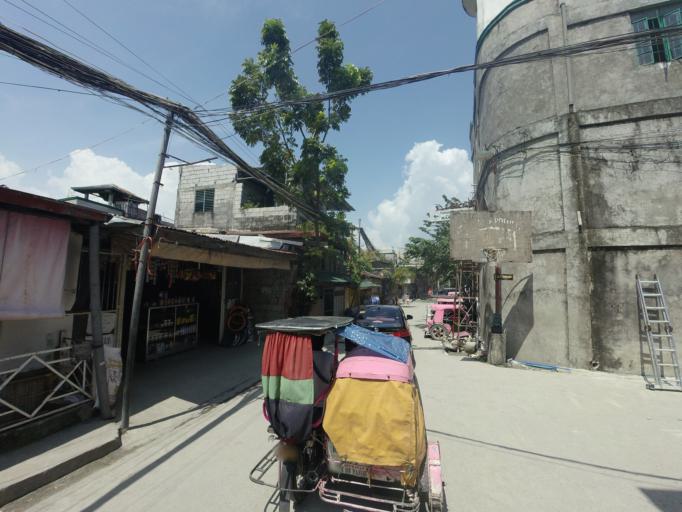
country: PH
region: Calabarzon
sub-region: Province of Rizal
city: Taguig
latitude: 14.5401
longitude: 121.1058
